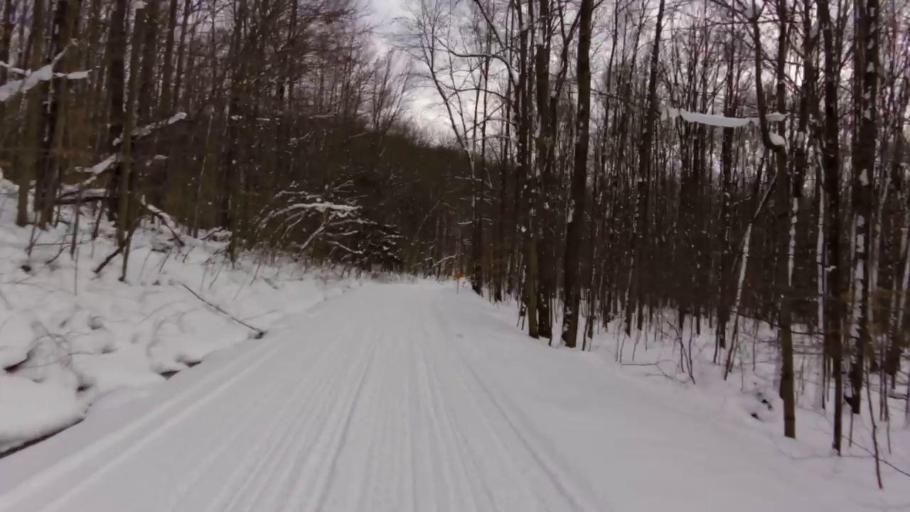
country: US
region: New York
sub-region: Cattaraugus County
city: Salamanca
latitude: 42.0524
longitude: -78.7546
